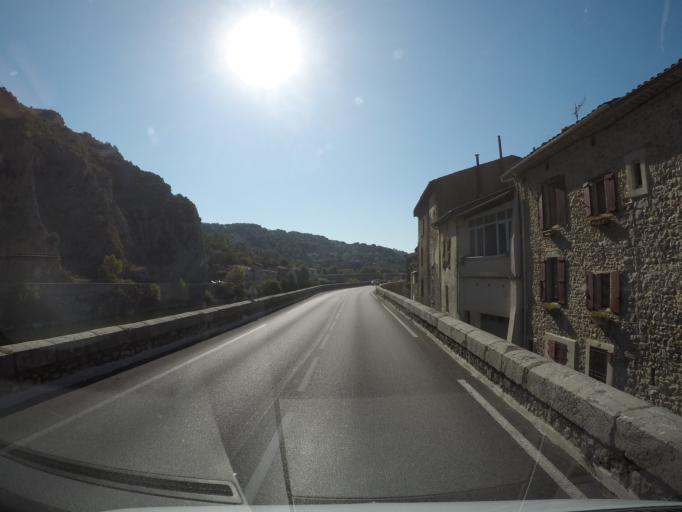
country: FR
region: Languedoc-Roussillon
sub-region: Departement du Gard
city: Anduze
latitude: 44.0589
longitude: 3.9855
